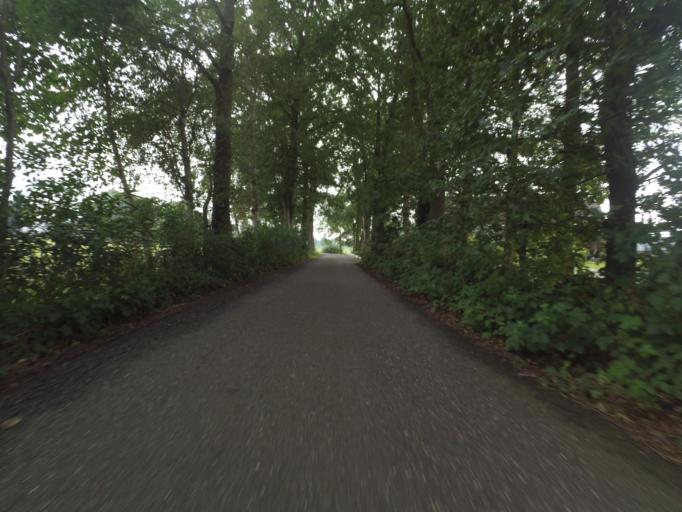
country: NL
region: Gelderland
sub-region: Gemeente Barneveld
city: Barneveld
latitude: 52.1298
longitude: 5.6264
